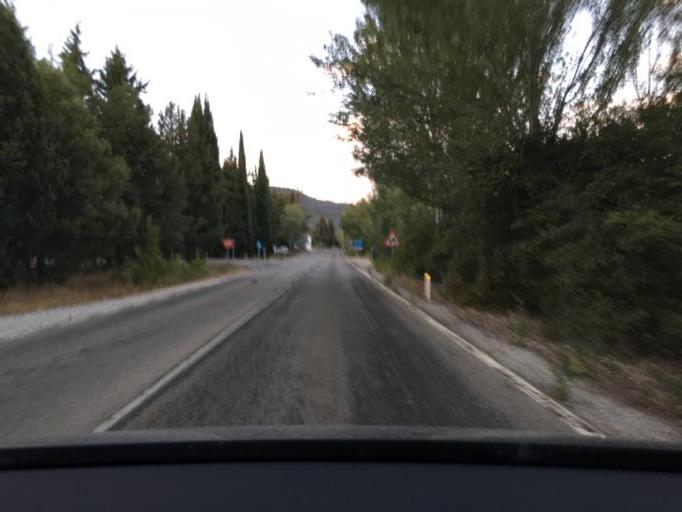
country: ES
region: Andalusia
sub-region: Provincia de Granada
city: Viznar
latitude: 37.2229
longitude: -3.5379
